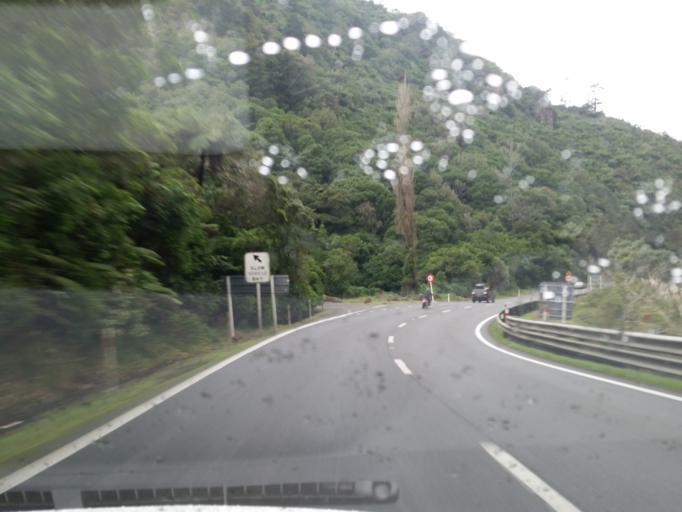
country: NZ
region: Waikato
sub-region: Hauraki District
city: Paeroa
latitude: -37.4230
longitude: 175.7250
